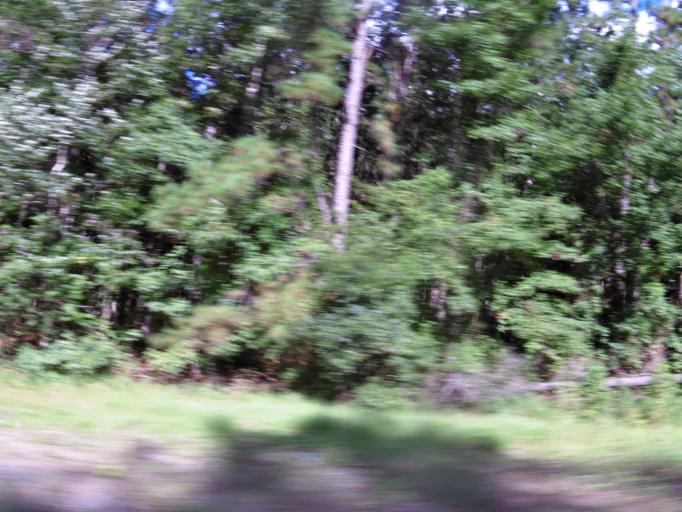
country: US
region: Georgia
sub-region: Camden County
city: Woodbine
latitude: 30.9028
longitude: -81.7104
